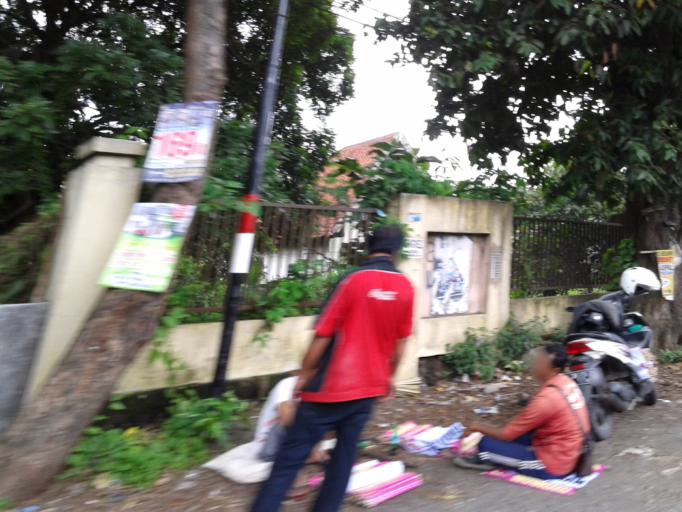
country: ID
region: East Java
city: Lawang
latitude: -7.8507
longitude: 112.6943
